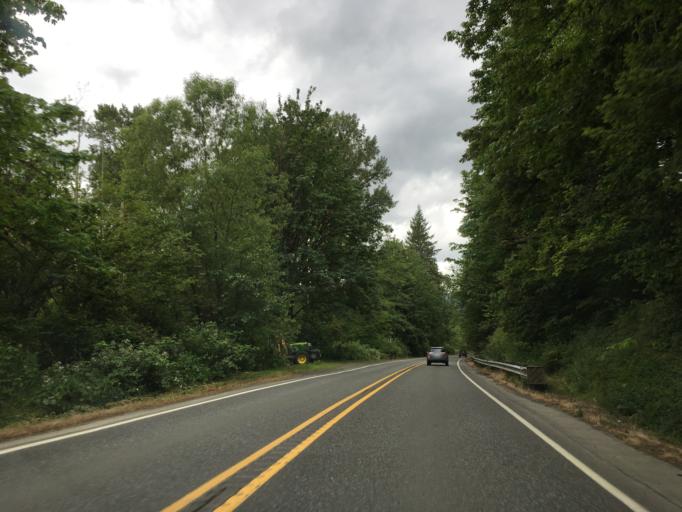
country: US
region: Washington
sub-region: Whatcom County
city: Peaceful Valley
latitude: 48.8222
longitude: -122.1885
